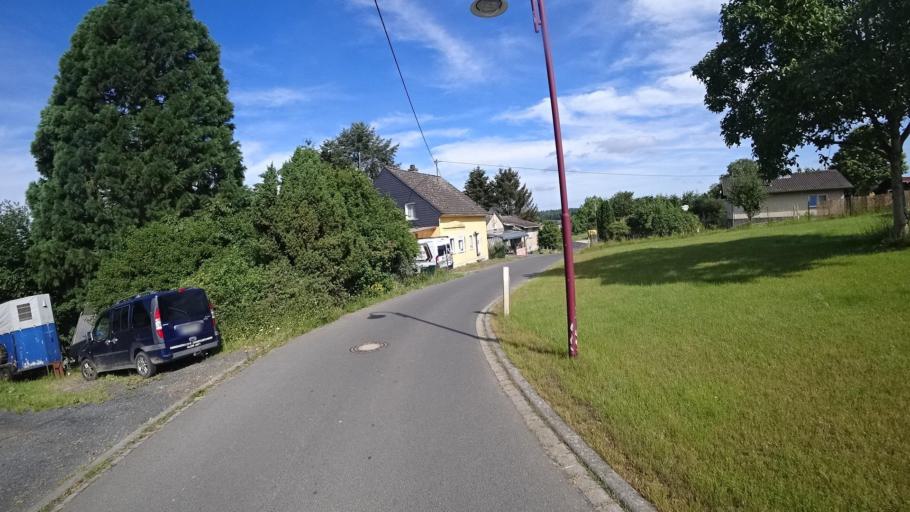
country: DE
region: Rheinland-Pfalz
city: Ratzert
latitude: 50.6469
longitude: 7.6303
